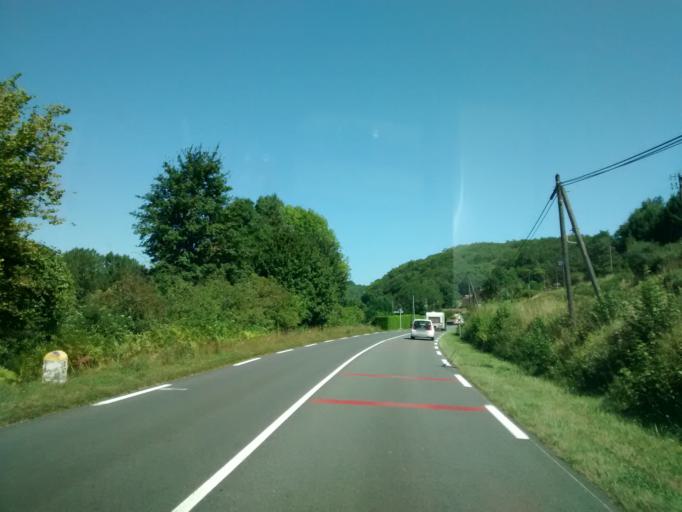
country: FR
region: Aquitaine
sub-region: Departement de la Dordogne
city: Le Bugue
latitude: 44.9603
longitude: 0.9872
